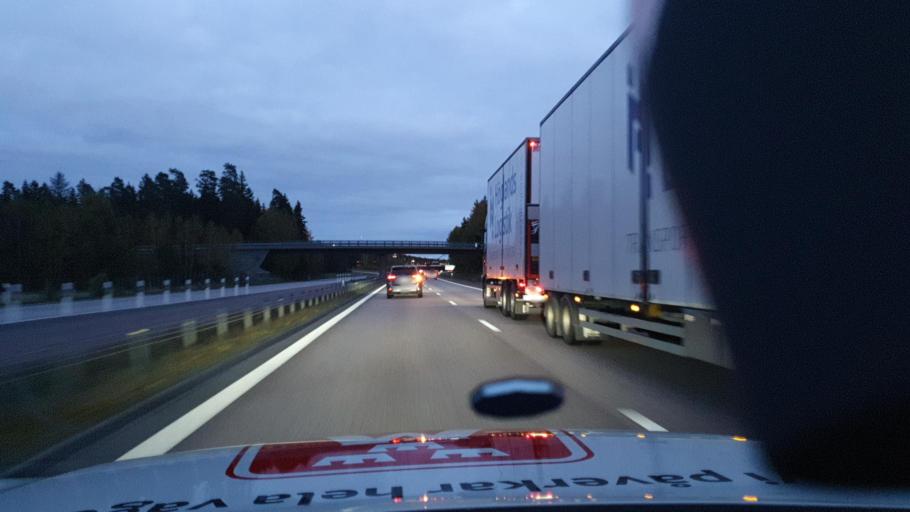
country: SE
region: Soedermanland
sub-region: Nykopings Kommun
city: Svalsta
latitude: 58.7511
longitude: 16.9101
